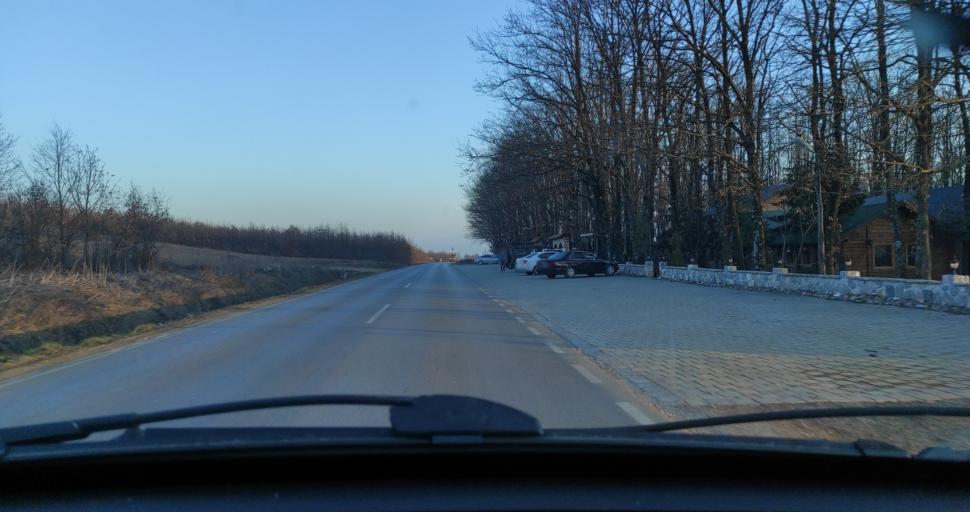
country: XK
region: Gjakova
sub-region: Komuna e Decanit
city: Gllogjan
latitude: 42.4575
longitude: 20.3541
